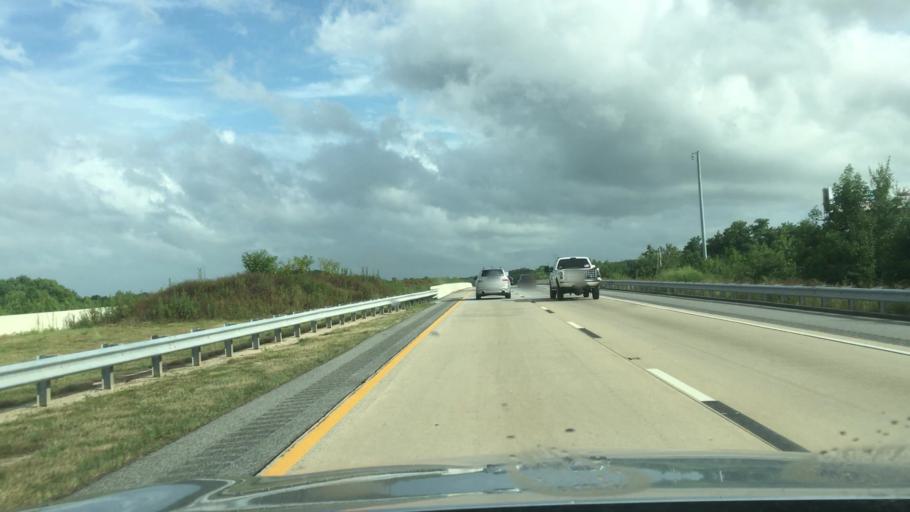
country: US
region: Delaware
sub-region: New Castle County
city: Townsend
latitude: 39.3866
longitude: -75.6649
